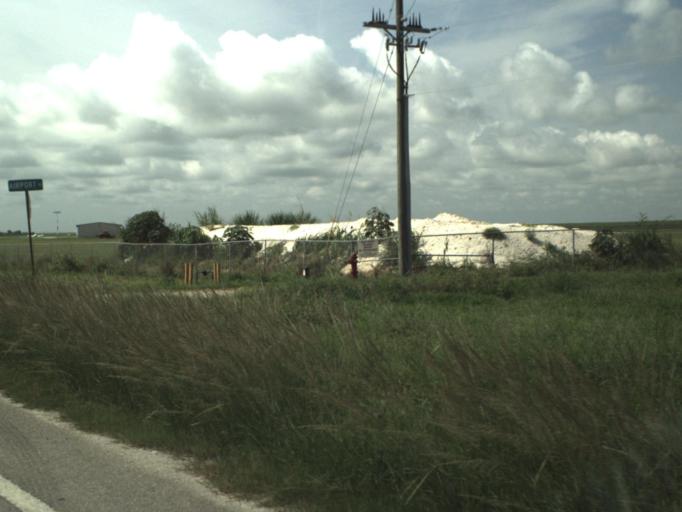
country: US
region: Florida
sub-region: Palm Beach County
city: Pahokee
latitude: 26.7932
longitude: -80.6928
